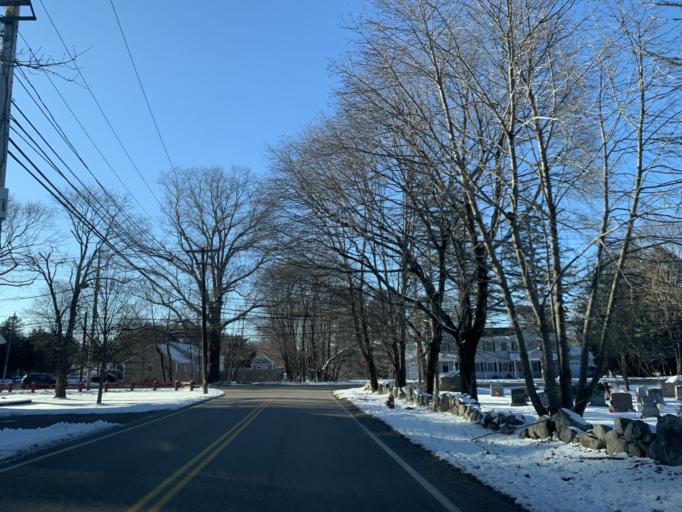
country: US
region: Massachusetts
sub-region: Norfolk County
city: Walpole
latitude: 42.1136
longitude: -71.2536
